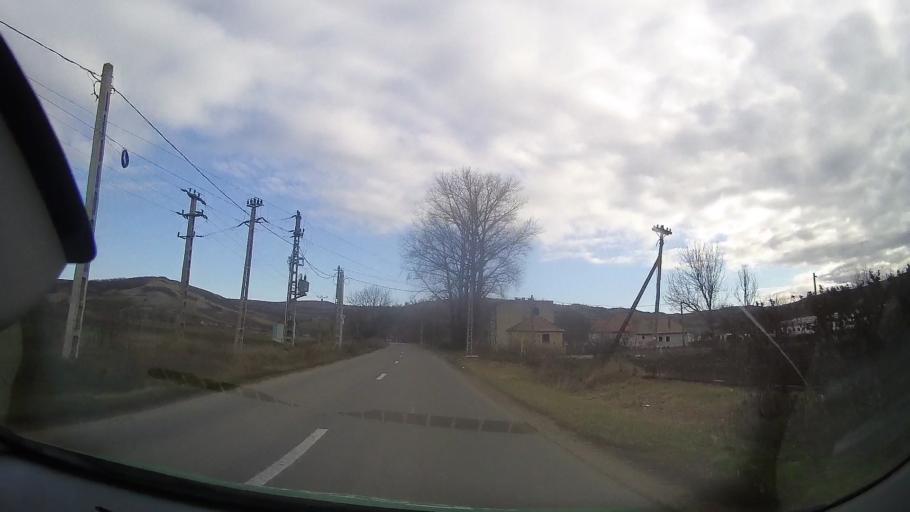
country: RO
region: Mures
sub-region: Comuna Iernut
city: Iernut
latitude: 46.4895
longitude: 24.2532
